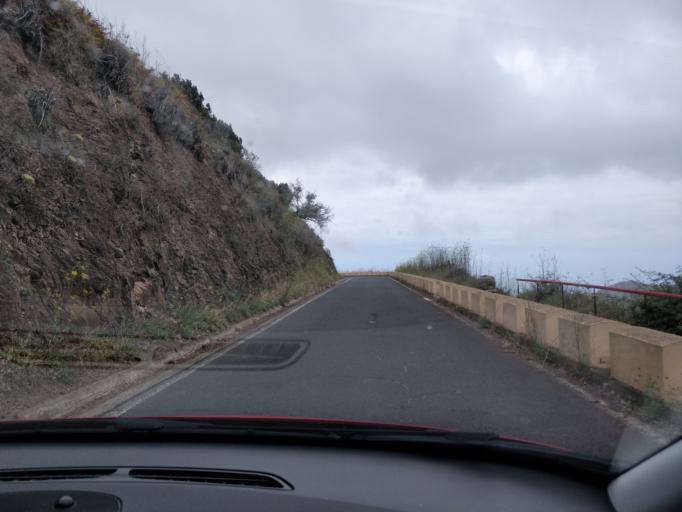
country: ES
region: Canary Islands
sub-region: Provincia de Santa Cruz de Tenerife
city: Santiago del Teide
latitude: 28.3232
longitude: -16.8507
